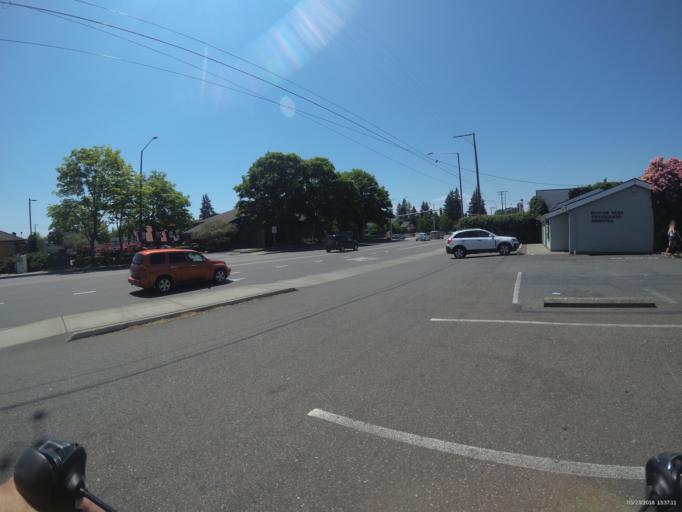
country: US
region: Washington
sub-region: Pierce County
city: Lakewood
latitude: 47.1672
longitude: -122.5192
